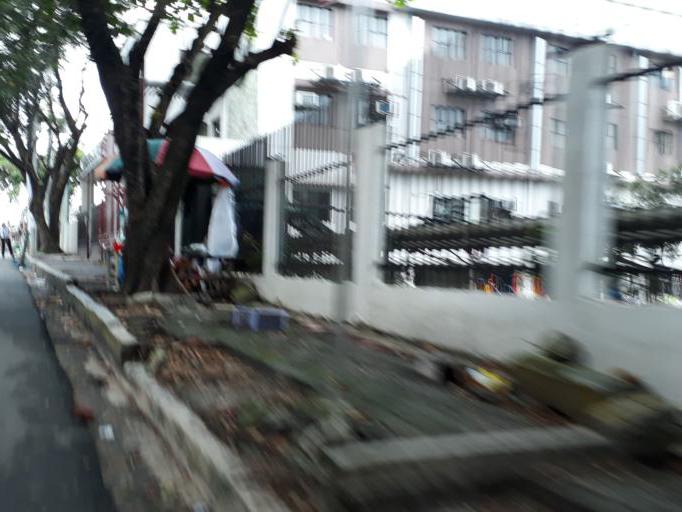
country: PH
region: Calabarzon
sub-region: Province of Rizal
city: Valenzuela
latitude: 14.6819
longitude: 120.9806
